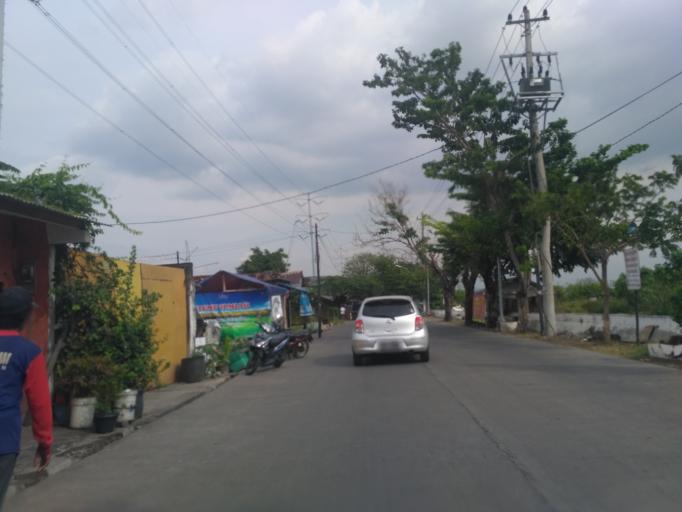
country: ID
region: Central Java
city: Semarang
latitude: -6.9698
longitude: 110.4017
